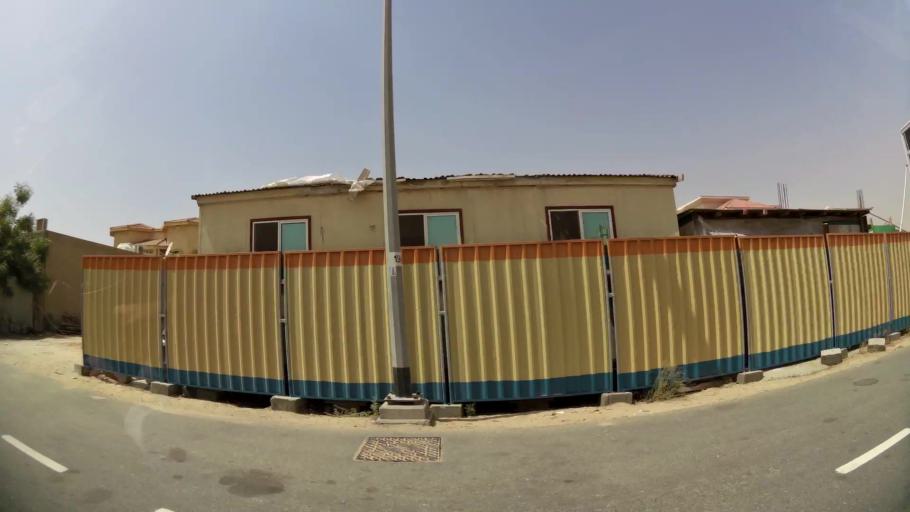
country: AE
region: Ash Shariqah
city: Sharjah
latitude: 25.2454
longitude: 55.4339
